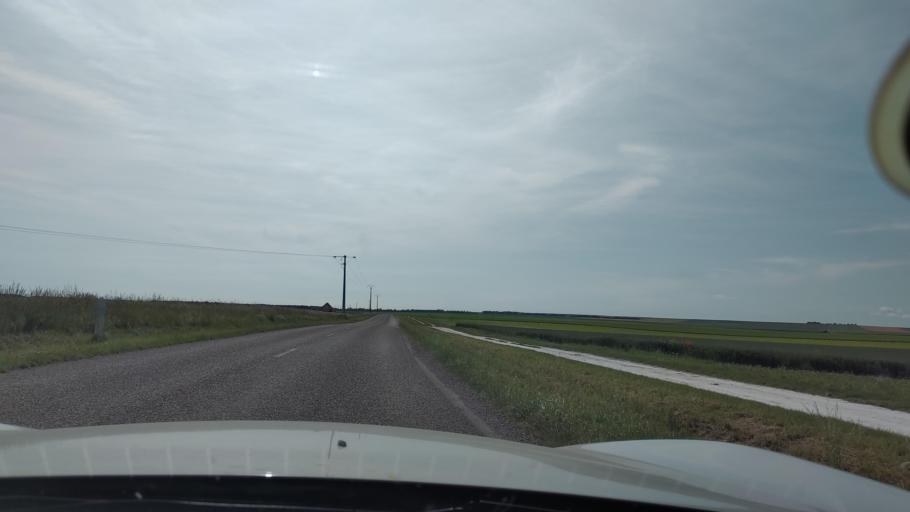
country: FR
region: Champagne-Ardenne
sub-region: Departement de l'Aube
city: Marigny-le-Chatel
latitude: 48.4020
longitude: 3.7673
